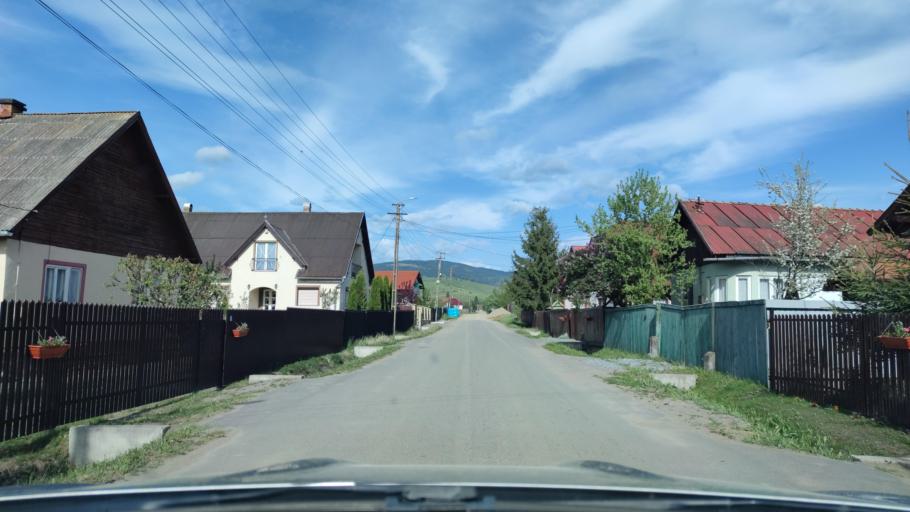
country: RO
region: Harghita
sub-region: Comuna Ditrau
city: Ditrau
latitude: 46.7948
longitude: 25.4887
